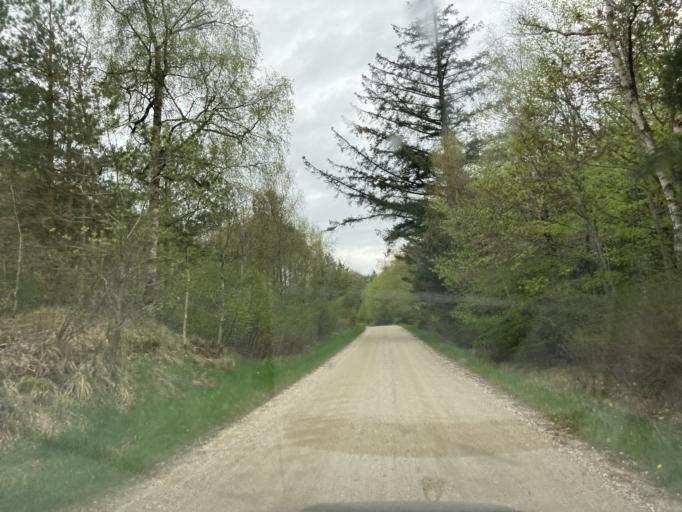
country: DK
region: North Denmark
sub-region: Thisted Kommune
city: Hanstholm
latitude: 57.0246
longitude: 8.5931
